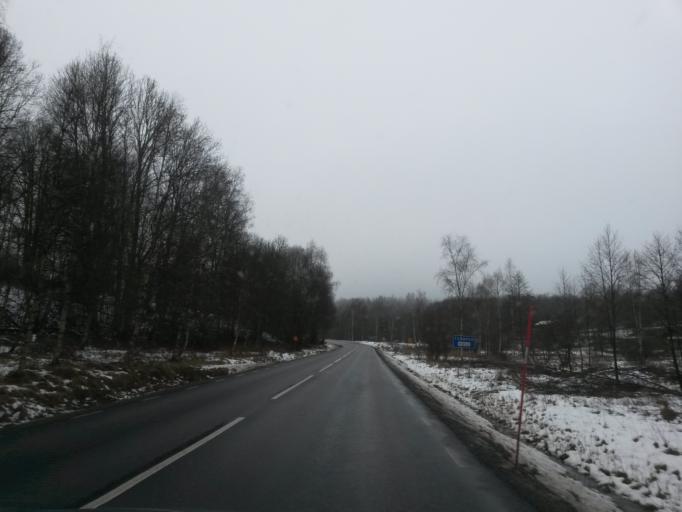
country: SE
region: Vaestra Goetaland
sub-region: Tranemo Kommun
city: Langhem
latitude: 57.6948
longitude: 13.3031
